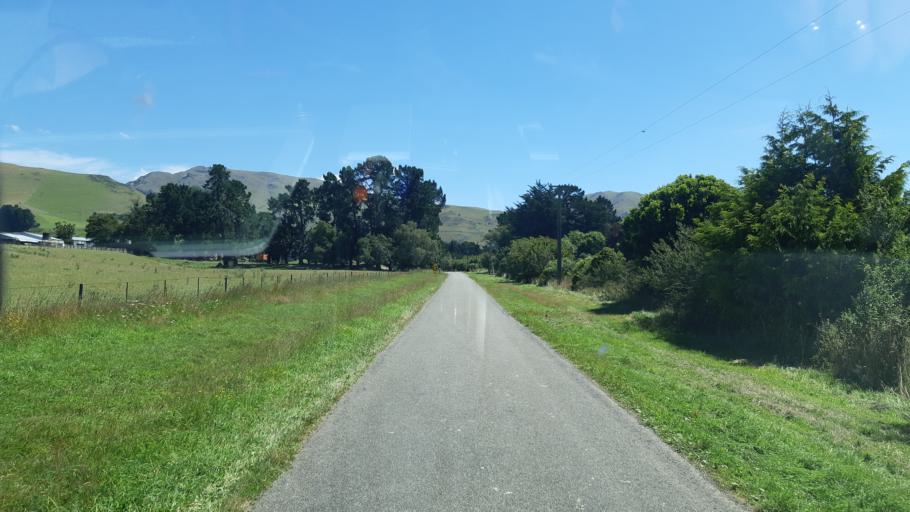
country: NZ
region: Canterbury
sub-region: Timaru District
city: Pleasant Point
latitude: -44.3328
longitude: 170.8776
